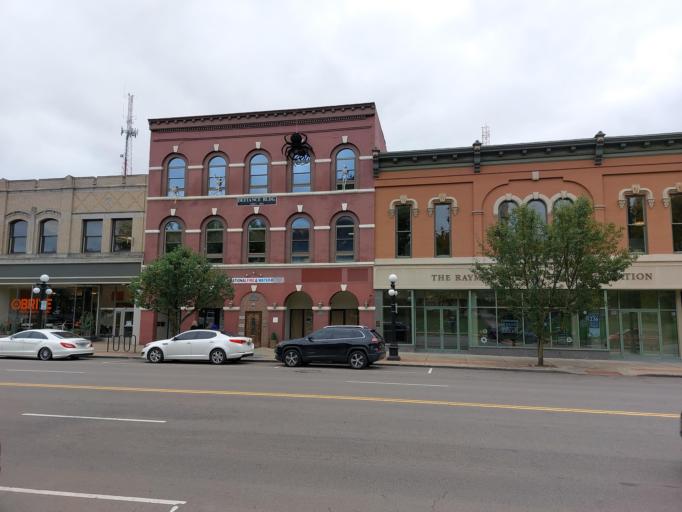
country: US
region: Ohio
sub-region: Trumbull County
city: Warren
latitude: 41.2362
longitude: -80.8189
